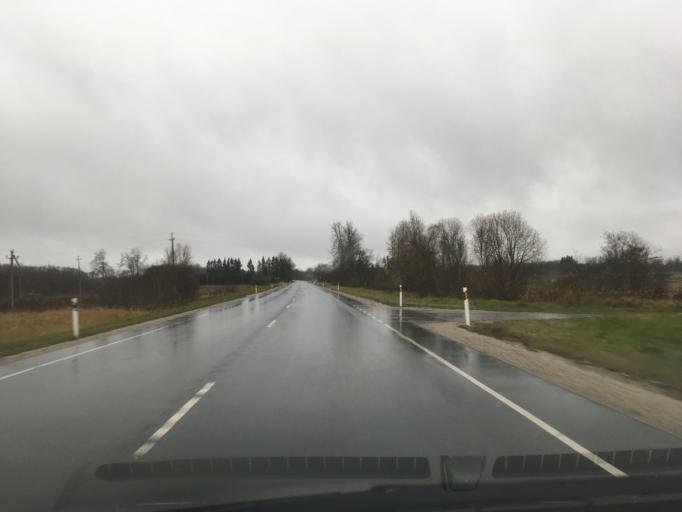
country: EE
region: Laeaene
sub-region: Lihula vald
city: Lihula
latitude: 58.8393
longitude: 24.0574
